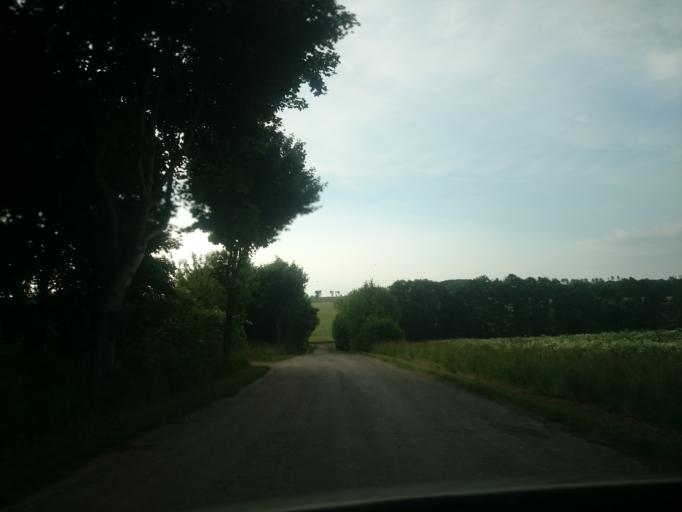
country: DE
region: Saxony
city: Eppendorf
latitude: 50.8318
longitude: 13.2357
